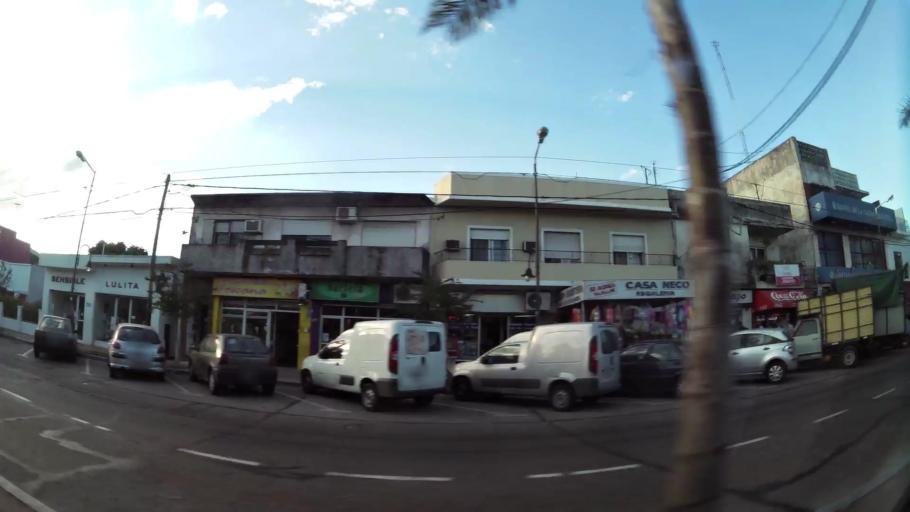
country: AR
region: Buenos Aires
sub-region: Partido de Tigre
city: Tigre
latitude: -34.4589
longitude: -58.5688
